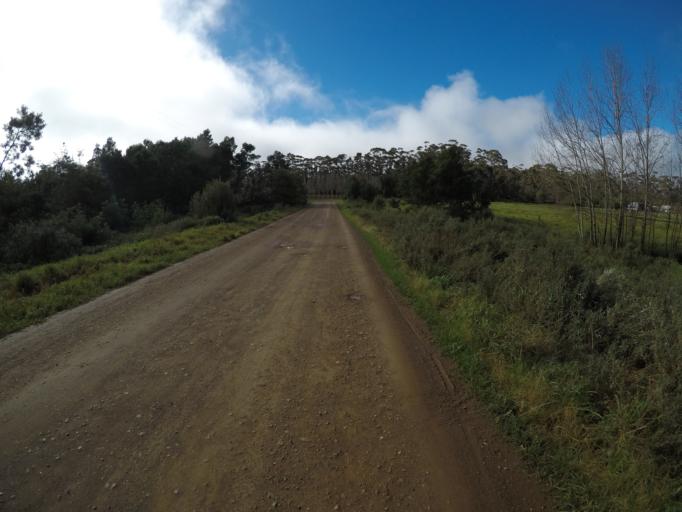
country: ZA
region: Western Cape
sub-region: Cape Winelands District Municipality
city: Ashton
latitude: -34.1117
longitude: 19.7958
